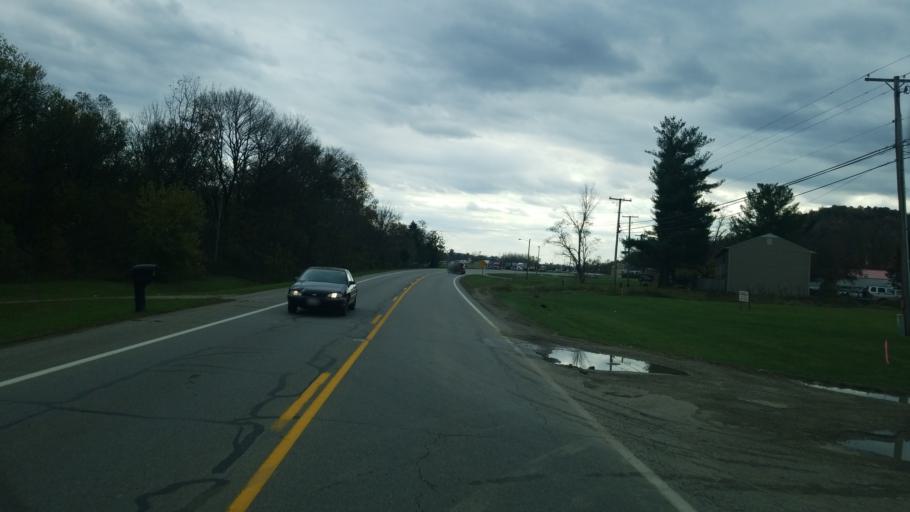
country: US
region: Ohio
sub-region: Scioto County
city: Lucasville
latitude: 38.8865
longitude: -83.0211
